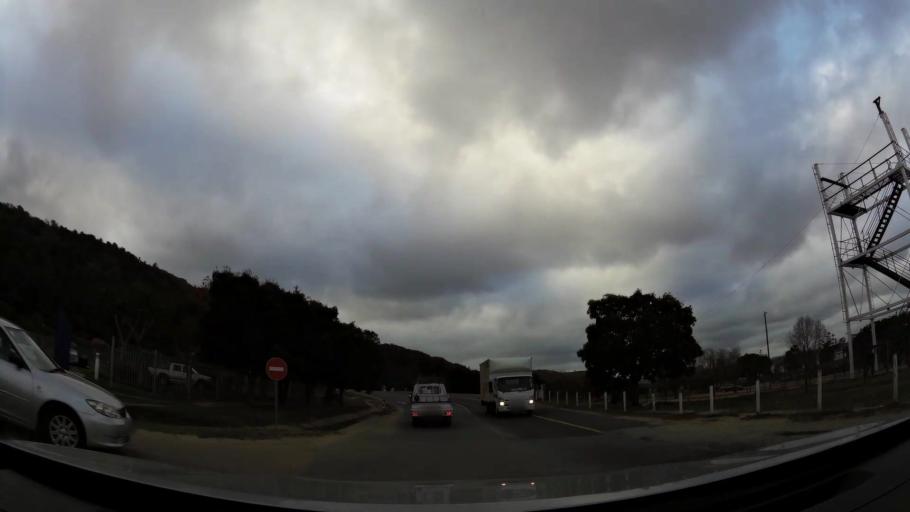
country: ZA
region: Western Cape
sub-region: Eden District Municipality
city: Plettenberg Bay
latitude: -34.0409
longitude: 23.3705
